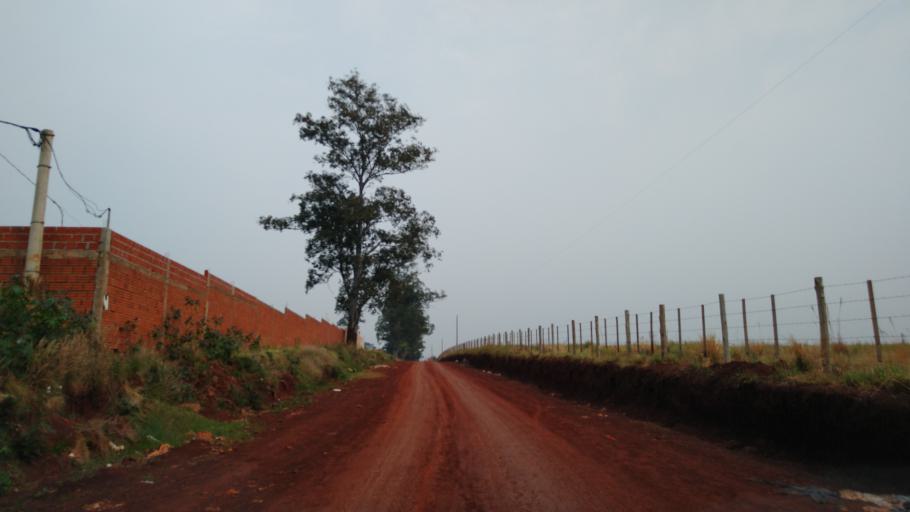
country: AR
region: Misiones
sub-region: Departamento de Capital
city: Posadas
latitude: -27.4477
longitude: -55.9340
